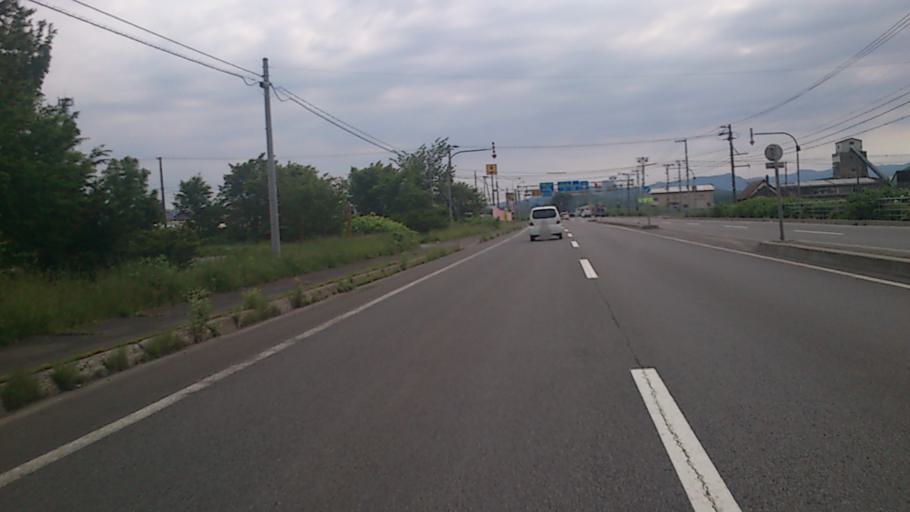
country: JP
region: Hokkaido
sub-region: Asahikawa-shi
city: Asahikawa
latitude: 43.8538
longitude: 142.5032
